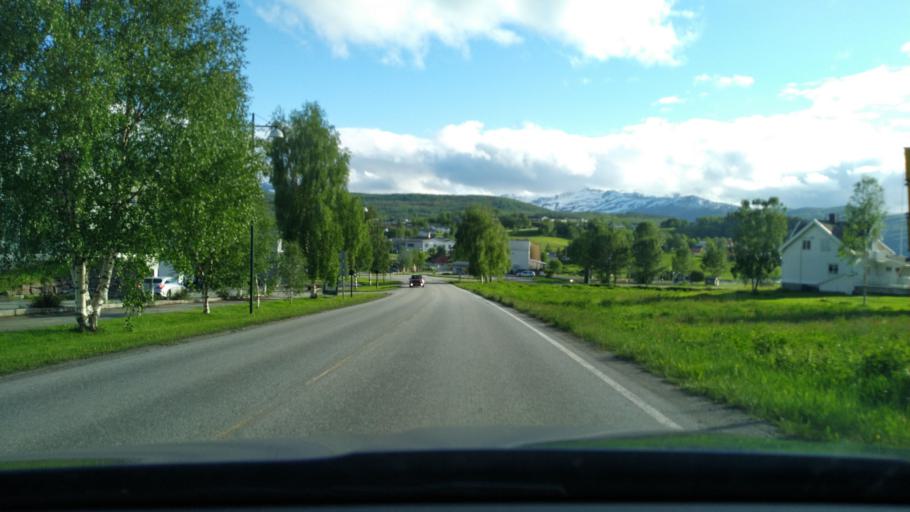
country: NO
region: Troms
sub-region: Sorreisa
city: Sorreisa
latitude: 69.1463
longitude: 18.1557
